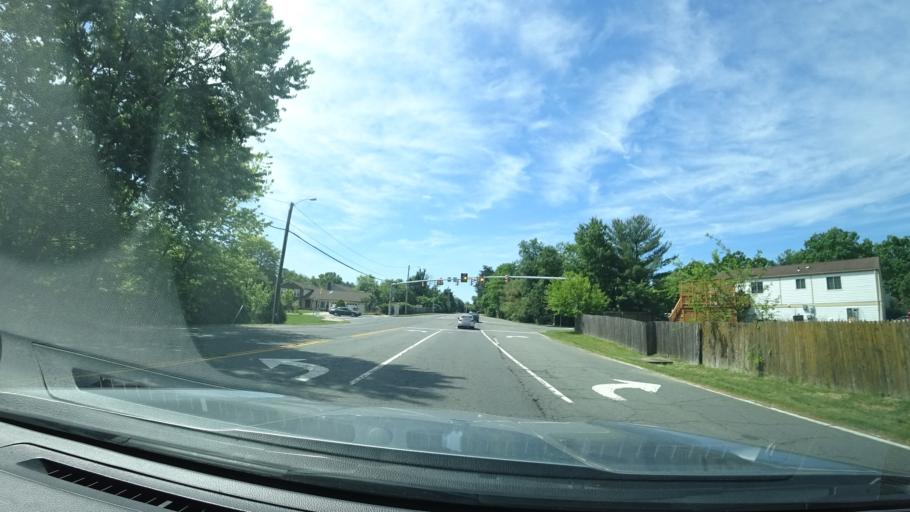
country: US
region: Virginia
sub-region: Loudoun County
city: Oak Grove
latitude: 38.9862
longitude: -77.3970
